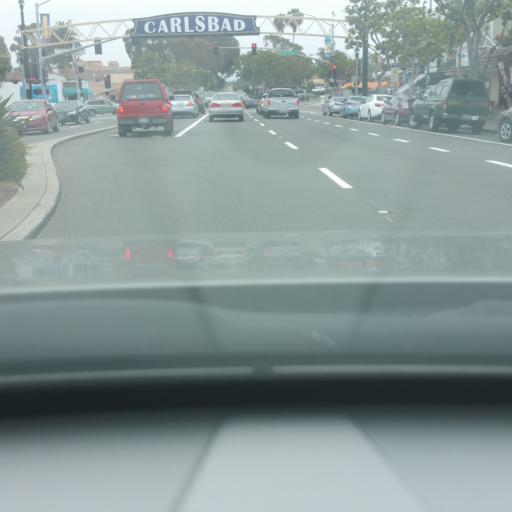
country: US
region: California
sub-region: San Diego County
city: Carlsbad
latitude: 33.1588
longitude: -117.3515
